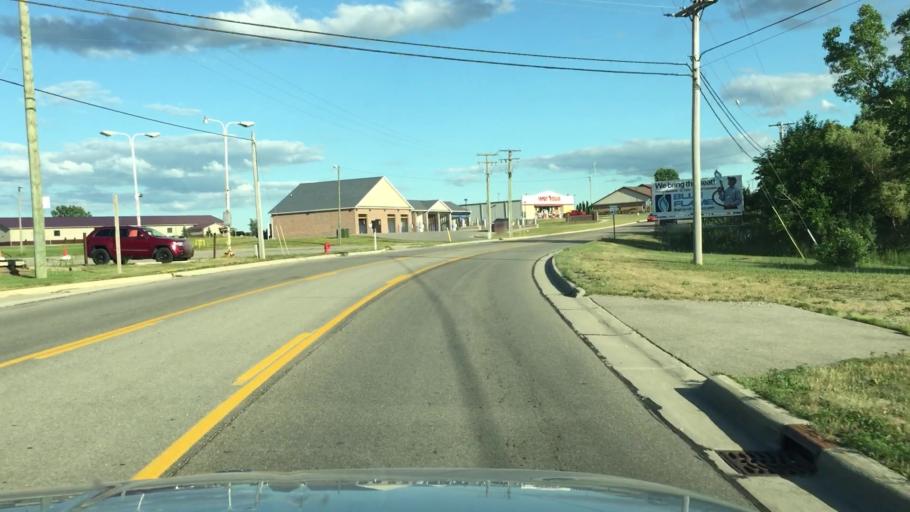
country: US
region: Michigan
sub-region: Saint Clair County
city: Yale
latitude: 43.1223
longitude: -82.7921
